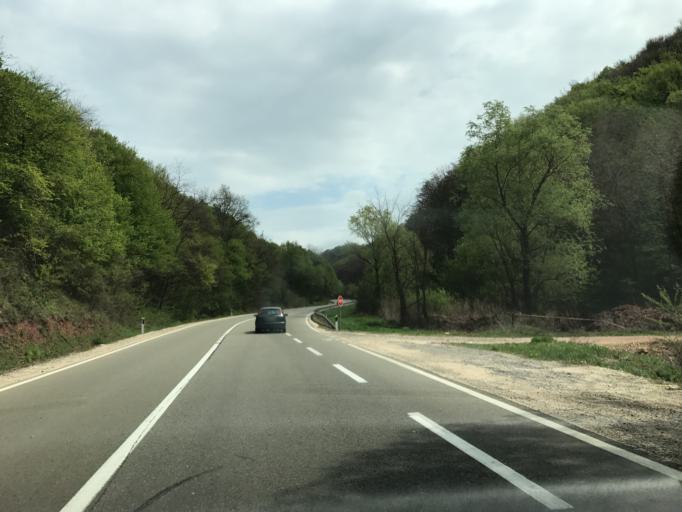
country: RS
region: Central Serbia
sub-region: Nisavski Okrug
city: Razanj
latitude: 43.8508
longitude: 21.6464
